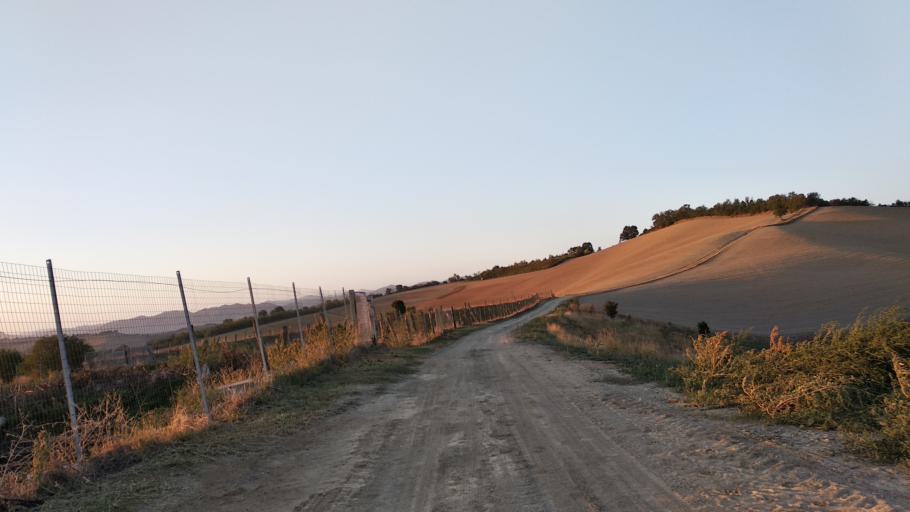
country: IT
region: Emilia-Romagna
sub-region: Provincia di Bologna
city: Dozza
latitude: 44.3420
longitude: 11.6003
